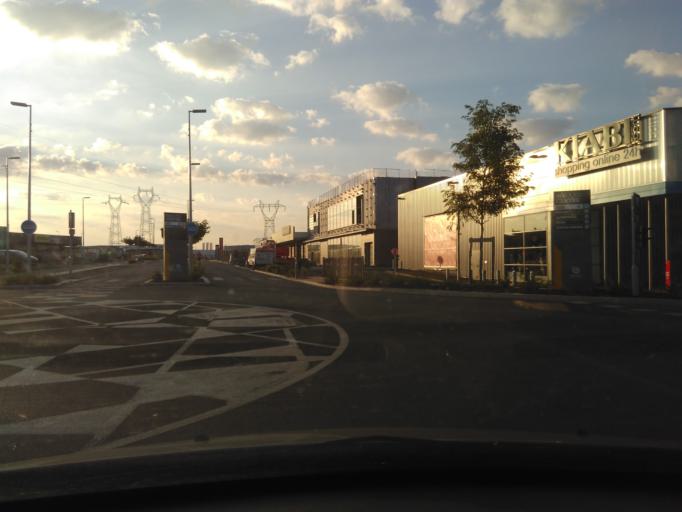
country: FR
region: Poitou-Charentes
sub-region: Departement de la Charente-Maritime
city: Puilboreau
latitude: 46.1761
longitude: -1.1137
